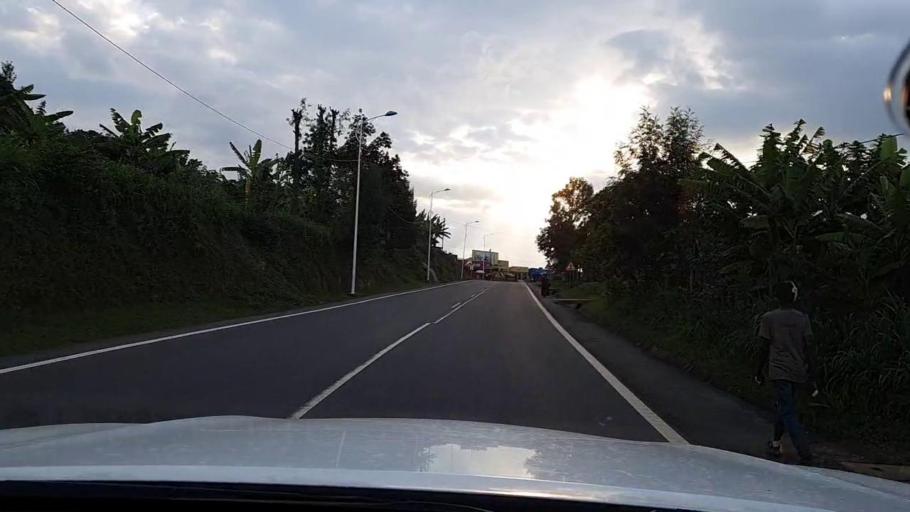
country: RW
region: Western Province
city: Kibuye
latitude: -2.0876
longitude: 29.4134
